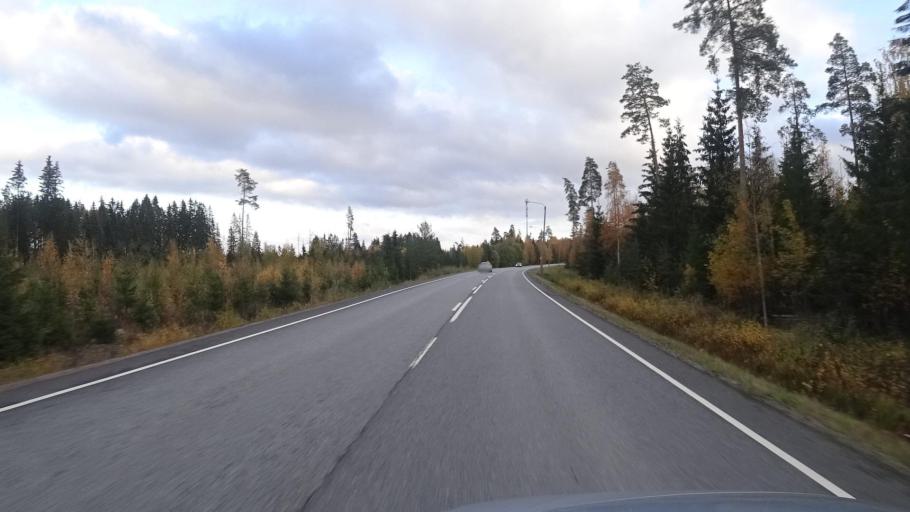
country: FI
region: Varsinais-Suomi
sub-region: Loimaa
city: Loimaa
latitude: 60.8801
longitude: 22.9866
